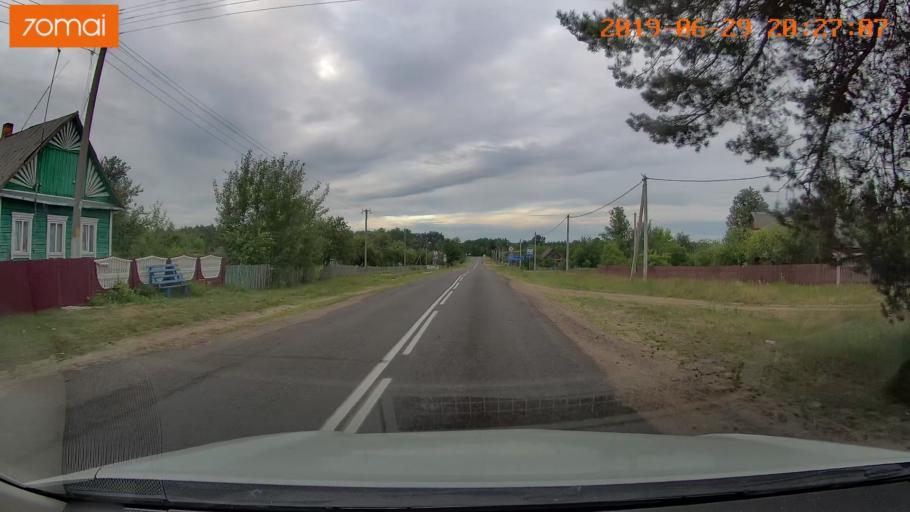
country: BY
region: Brest
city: Hantsavichy
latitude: 52.4716
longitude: 26.3017
